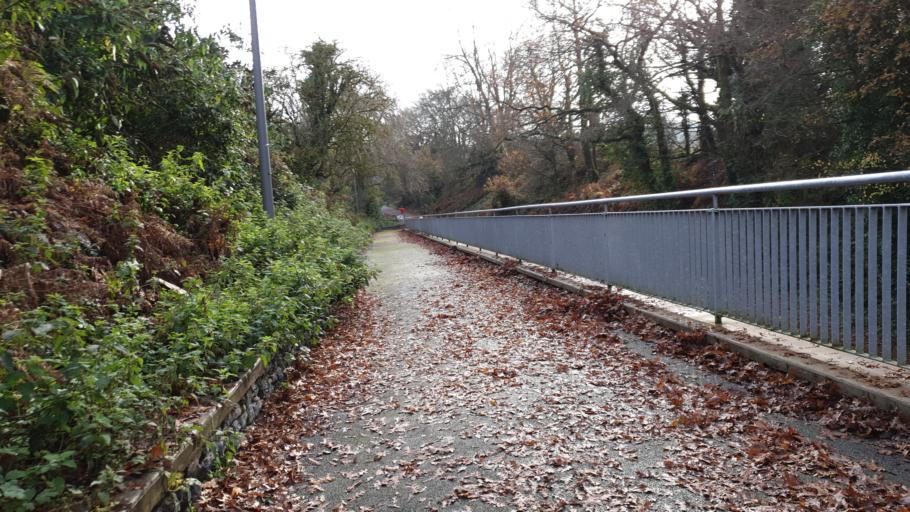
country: IE
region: Munster
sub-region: County Cork
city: Passage West
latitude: 51.8855
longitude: -8.4063
